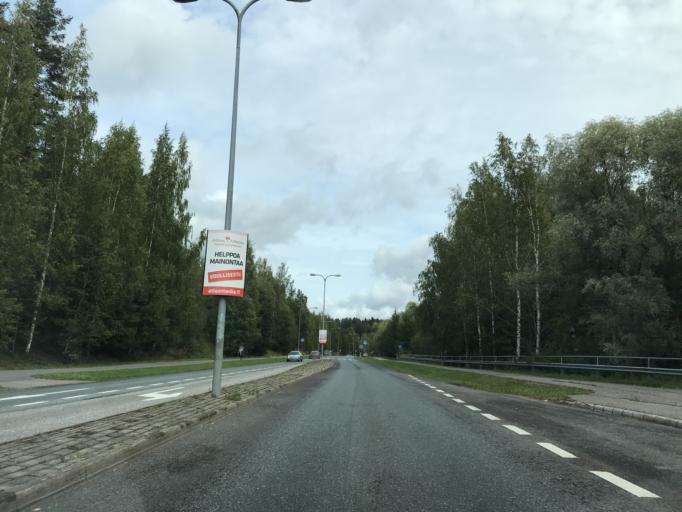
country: FI
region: Paijanne Tavastia
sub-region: Lahti
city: Lahti
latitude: 60.9930
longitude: 25.7469
